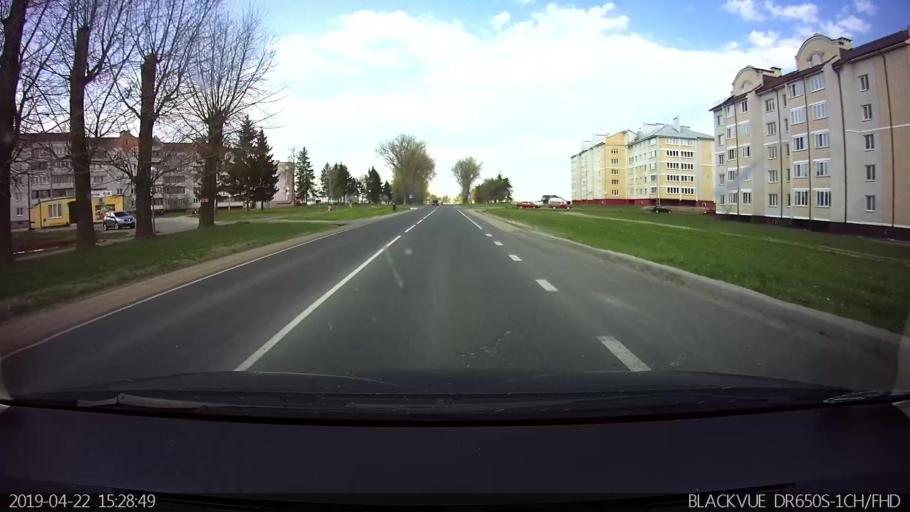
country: BY
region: Brest
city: Vysokaye
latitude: 52.3780
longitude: 23.3681
